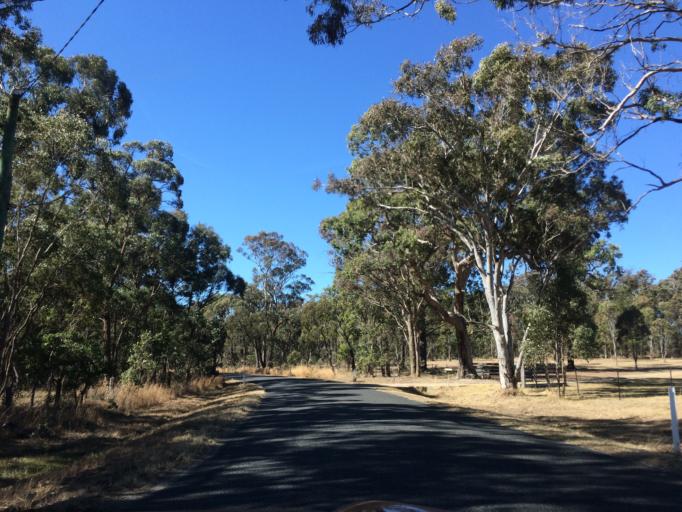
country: AU
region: Queensland
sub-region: Southern Downs
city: Stanthorpe
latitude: -28.6931
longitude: 152.0221
